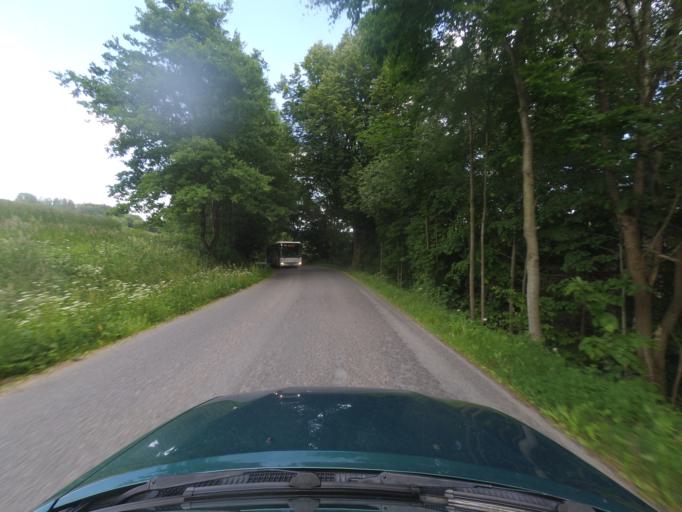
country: CZ
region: Pardubicky
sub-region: Okres Usti nad Orlici
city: Kunvald
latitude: 50.1159
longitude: 16.5854
